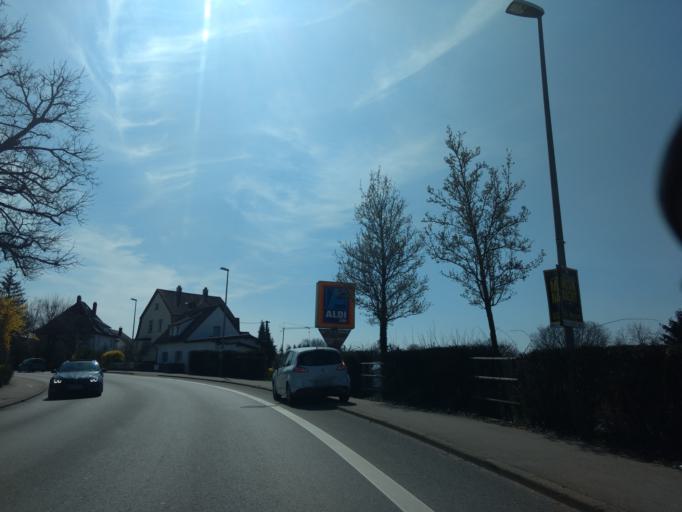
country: DE
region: Baden-Wuerttemberg
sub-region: Regierungsbezirk Stuttgart
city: Rechberghausen
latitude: 48.7272
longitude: 9.6417
